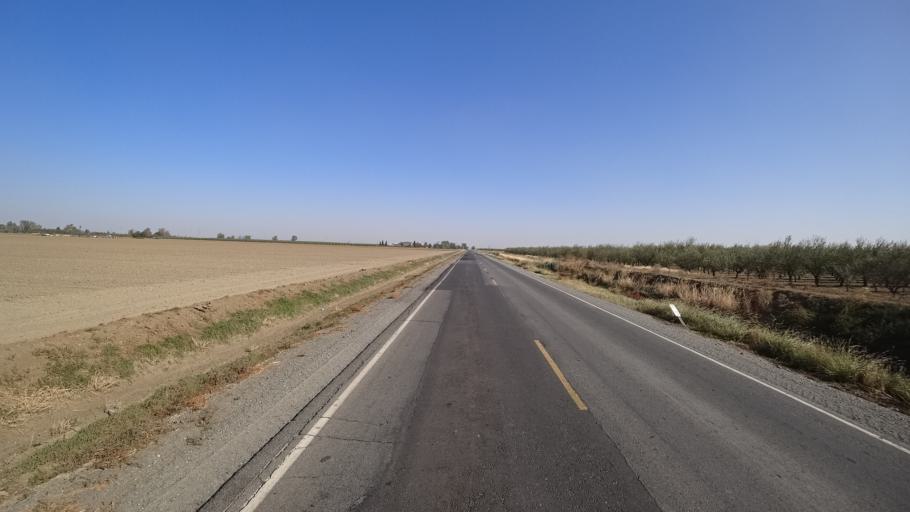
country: US
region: California
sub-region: Yolo County
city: Esparto
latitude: 38.7321
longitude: -121.9968
